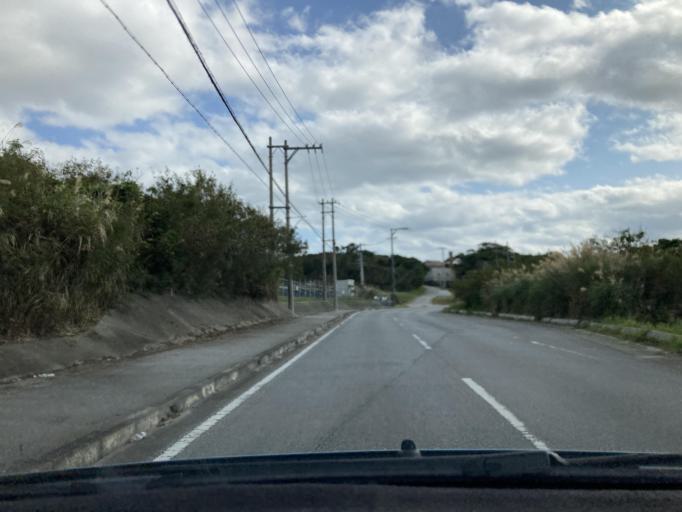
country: JP
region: Okinawa
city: Tomigusuku
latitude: 26.1695
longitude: 127.7642
